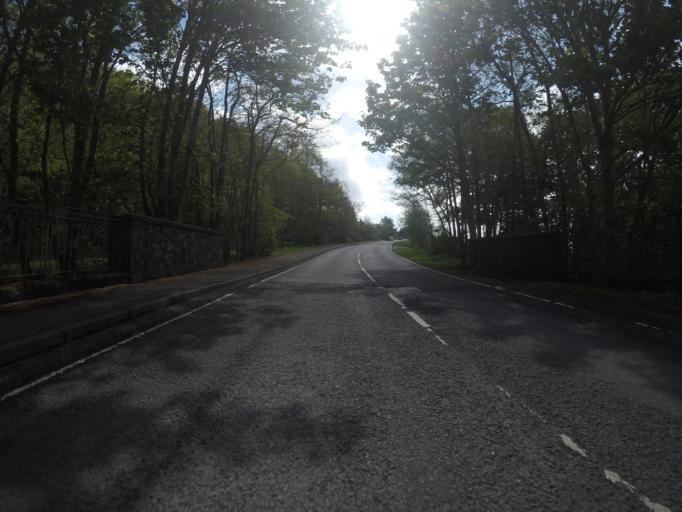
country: GB
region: Scotland
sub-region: Highland
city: Portree
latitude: 57.5891
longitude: -6.3550
